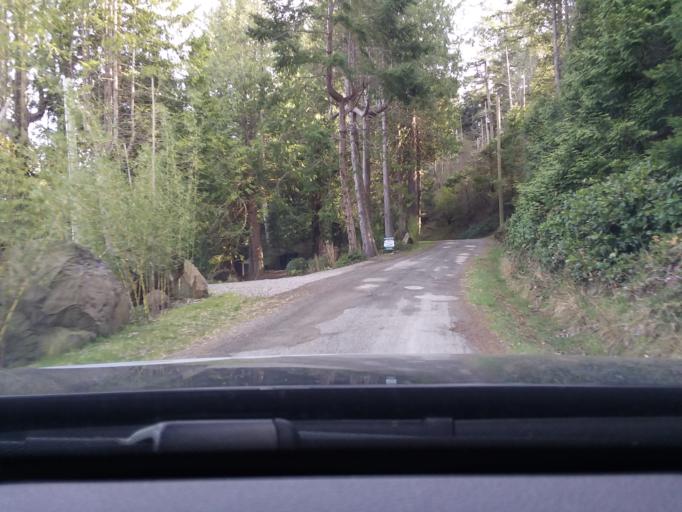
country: CA
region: British Columbia
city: North Saanich
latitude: 48.7415
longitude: -123.2377
